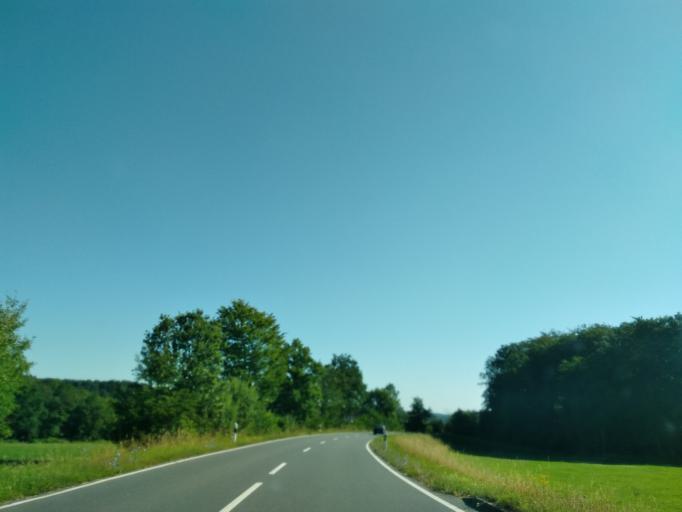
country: DE
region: Baden-Wuerttemberg
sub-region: Karlsruhe Region
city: Limbach
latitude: 49.4961
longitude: 9.2575
